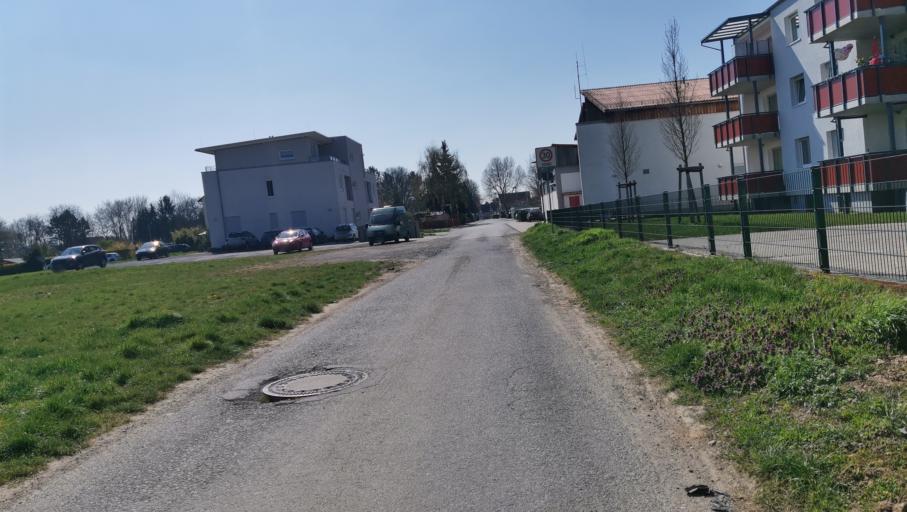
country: DE
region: Hesse
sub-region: Regierungsbezirk Darmstadt
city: Karben
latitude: 50.2094
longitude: 8.7583
